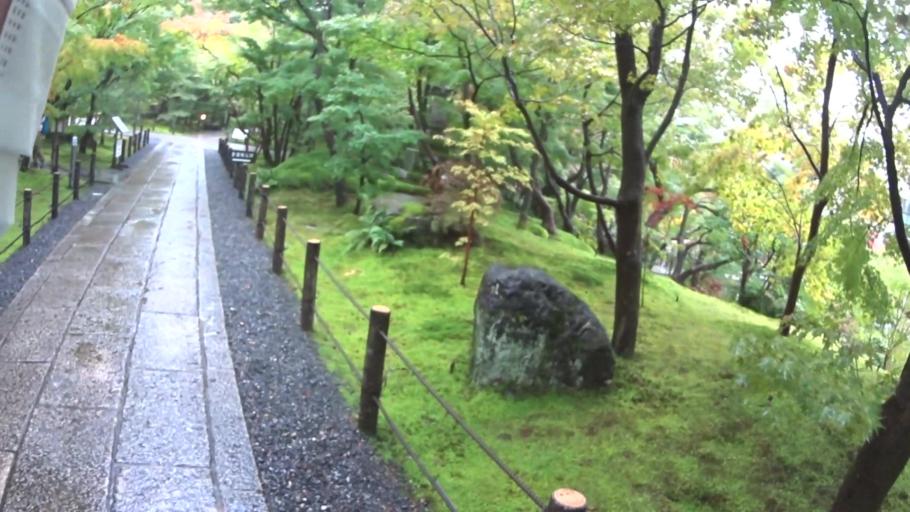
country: JP
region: Shiga Prefecture
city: Otsu-shi
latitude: 34.9789
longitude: 135.8120
